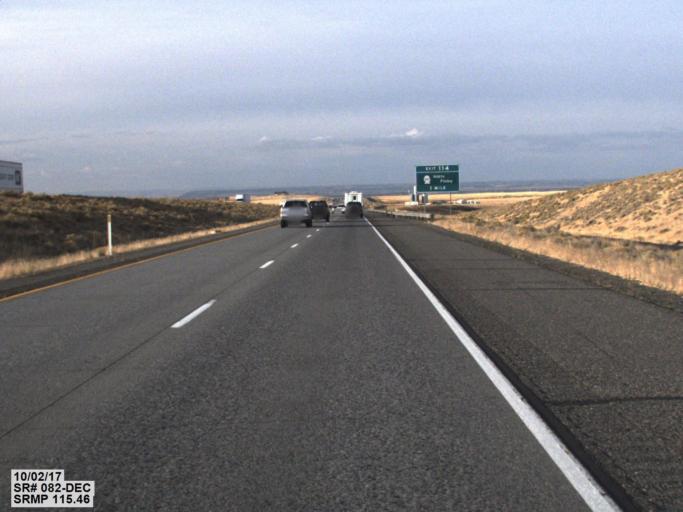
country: US
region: Washington
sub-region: Benton County
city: Highland
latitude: 46.1270
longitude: -119.2020
